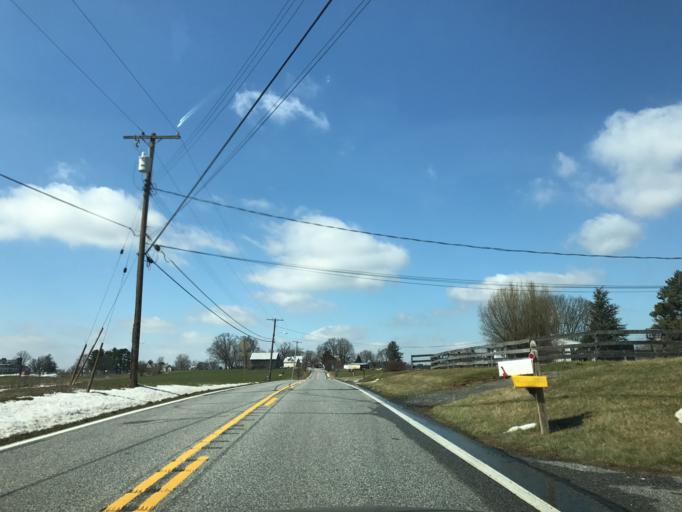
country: US
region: Maryland
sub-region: Carroll County
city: Hampstead
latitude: 39.5979
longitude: -76.7714
